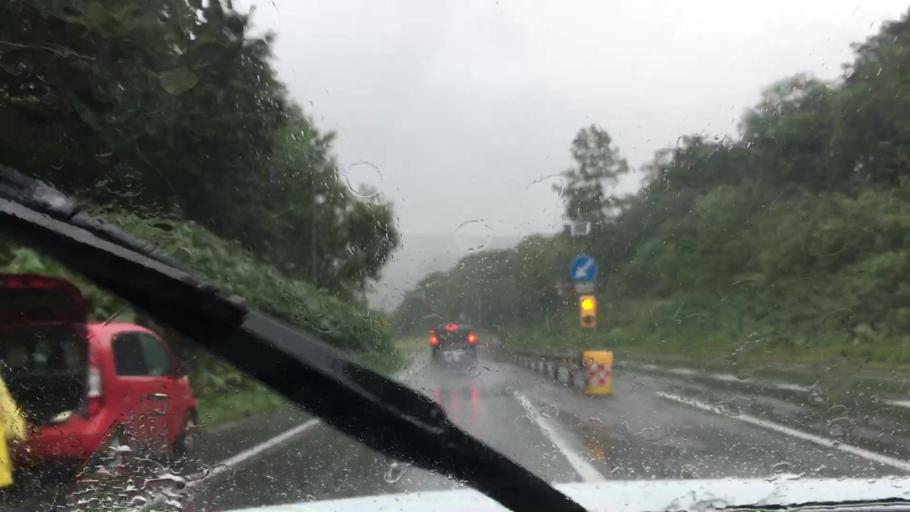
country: JP
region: Hokkaido
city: Sapporo
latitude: 42.8506
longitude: 141.0808
